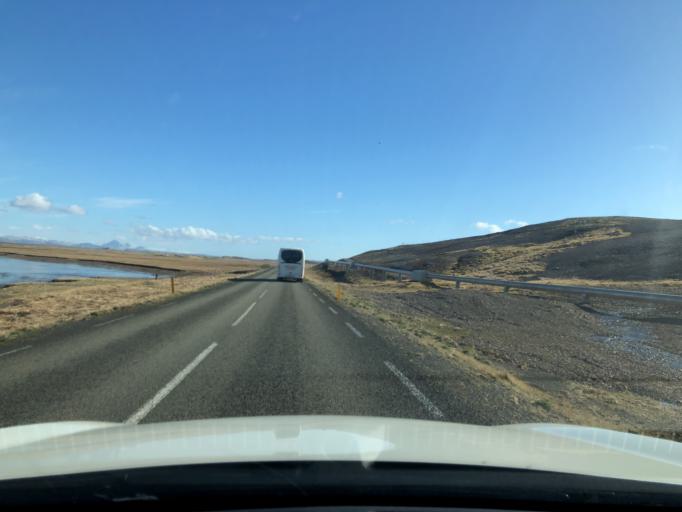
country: IS
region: West
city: Borgarnes
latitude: 64.5347
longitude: -21.7684
